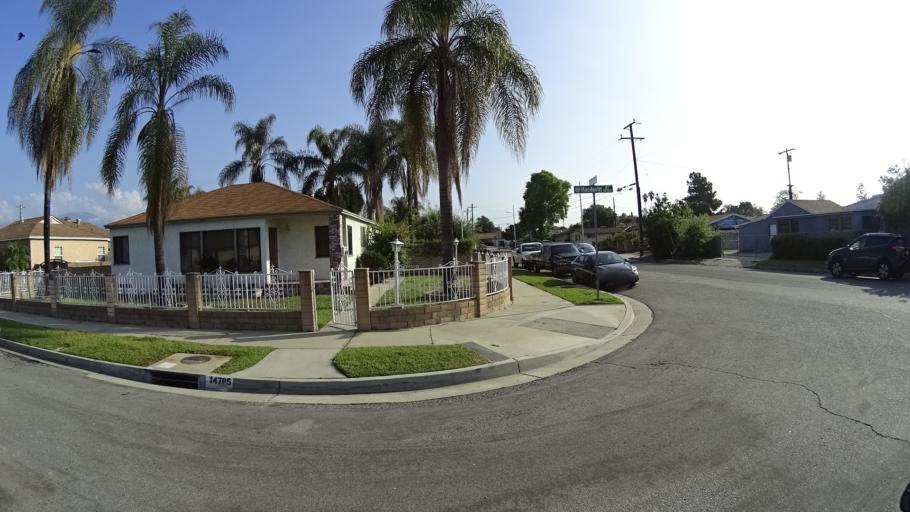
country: US
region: California
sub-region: Los Angeles County
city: Baldwin Park
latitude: 34.0736
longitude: -117.9544
